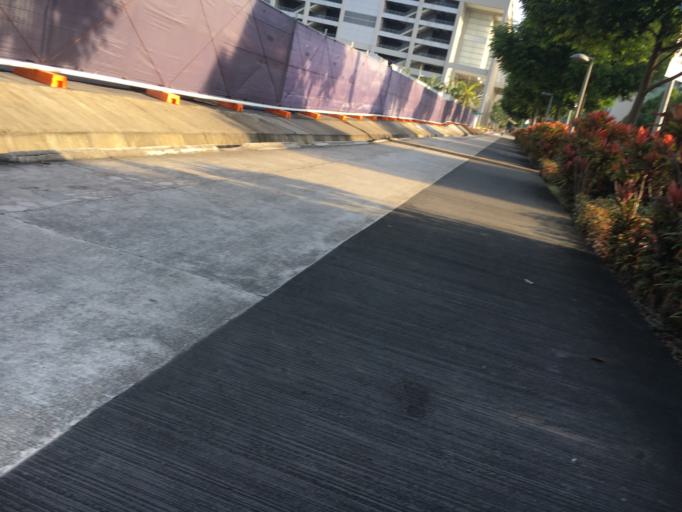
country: SG
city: Singapore
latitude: 1.2801
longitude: 103.8577
